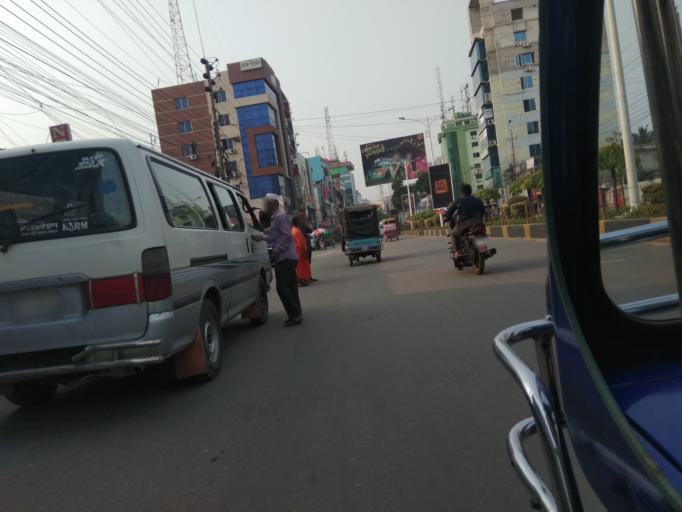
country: BD
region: Khulna
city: Khulna
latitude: 22.8184
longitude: 89.5532
